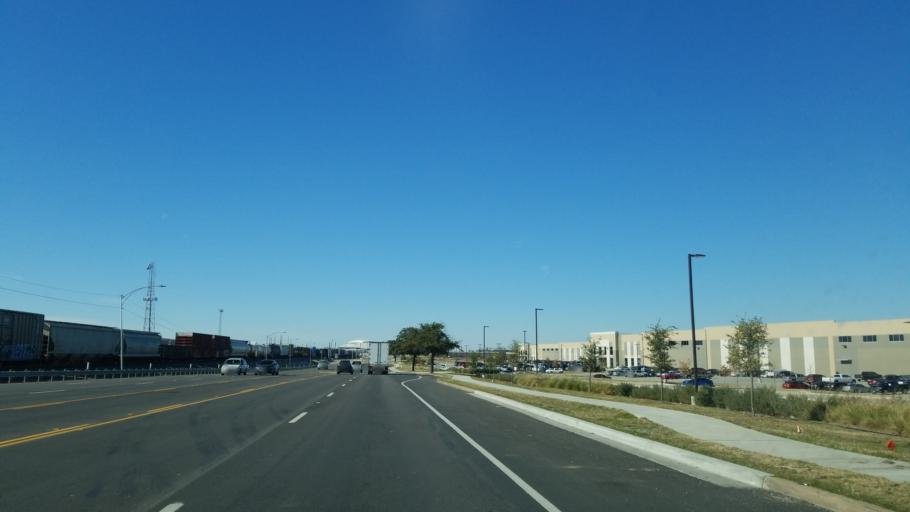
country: US
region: Texas
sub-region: Tarrant County
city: Arlington
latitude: 32.7412
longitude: -97.0543
